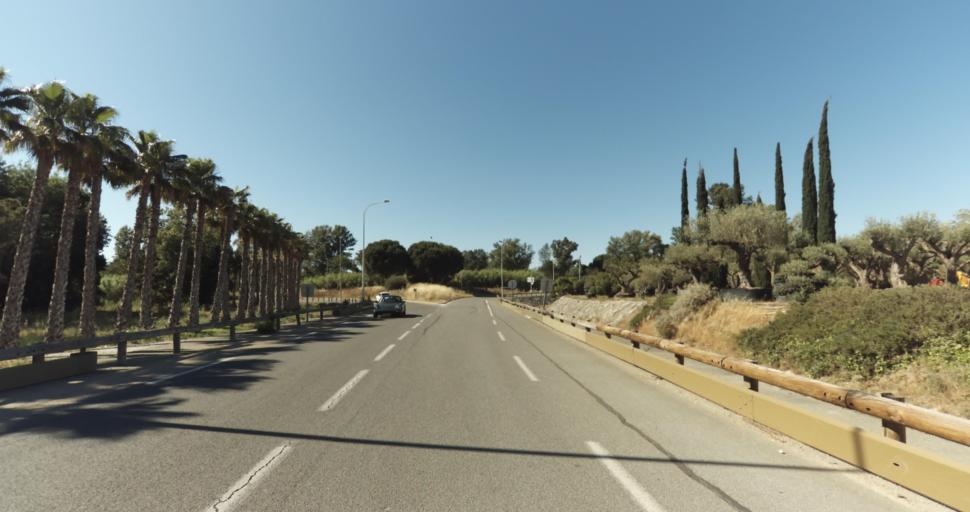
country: FR
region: Provence-Alpes-Cote d'Azur
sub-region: Departement du Var
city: Gassin
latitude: 43.2587
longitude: 6.5924
